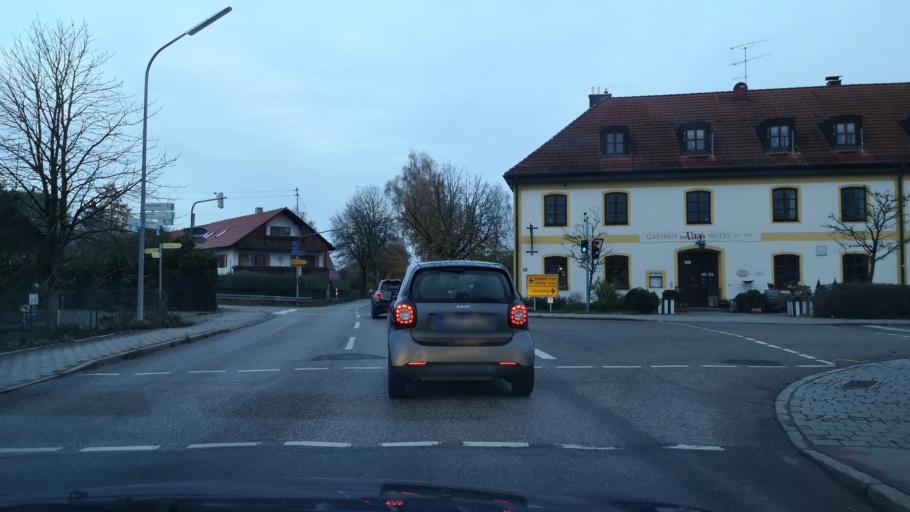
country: DE
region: Bavaria
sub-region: Upper Bavaria
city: Forstinning
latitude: 48.1595
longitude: 11.8990
